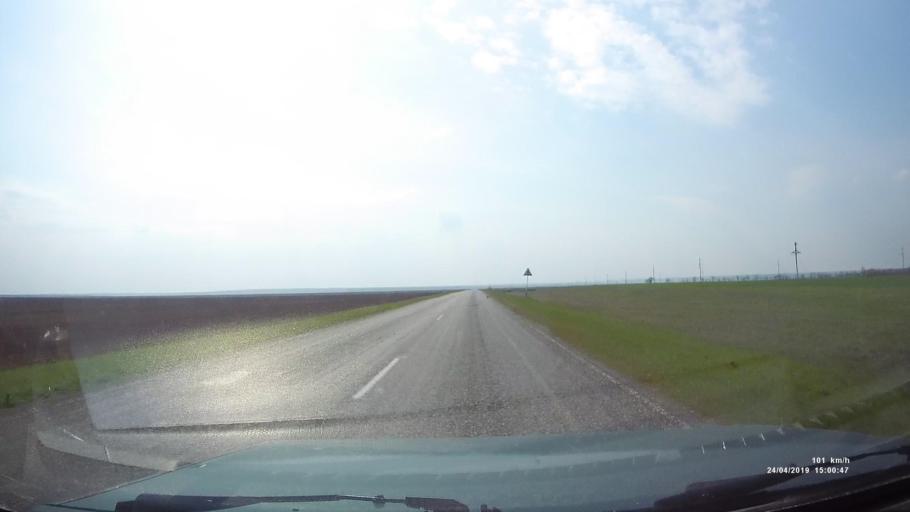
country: RU
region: Rostov
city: Remontnoye
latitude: 46.5654
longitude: 43.5482
